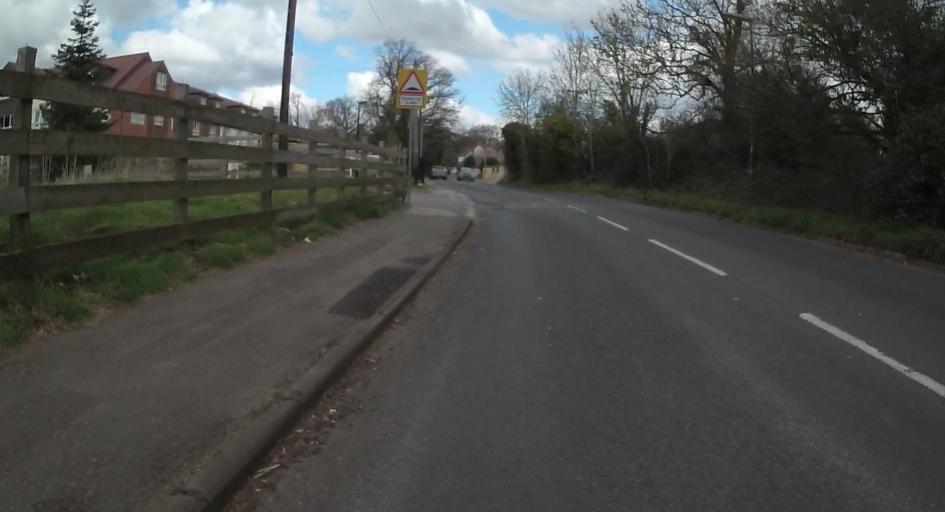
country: GB
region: England
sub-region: Surrey
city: Ottershaw
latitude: 51.3560
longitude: -0.5138
